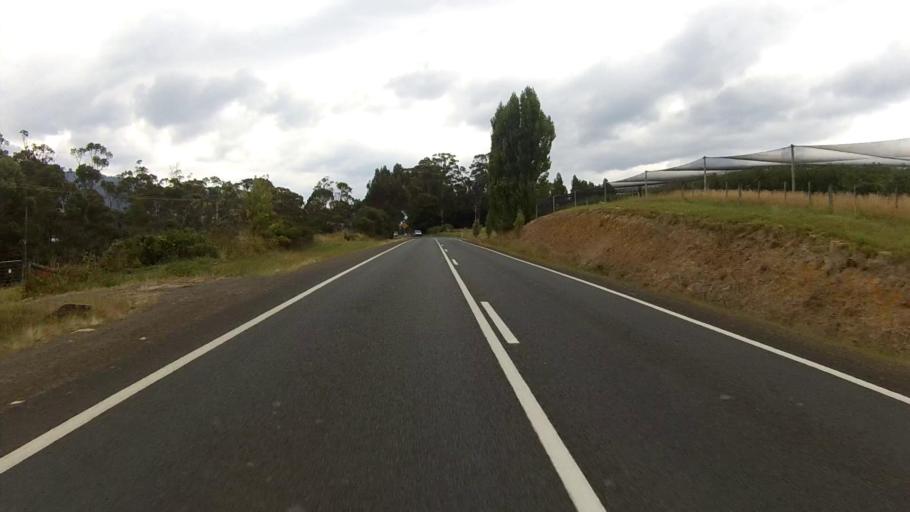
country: AU
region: Tasmania
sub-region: Huon Valley
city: Franklin
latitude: -43.0793
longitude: 147.0323
